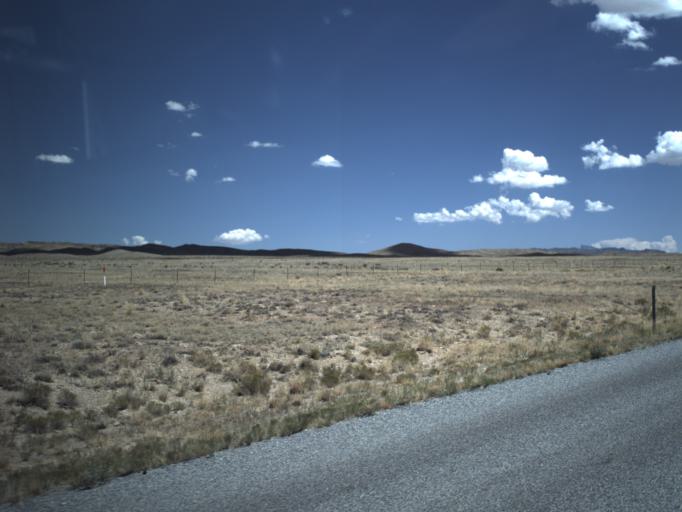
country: US
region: Nevada
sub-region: White Pine County
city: McGill
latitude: 39.0412
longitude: -113.8414
